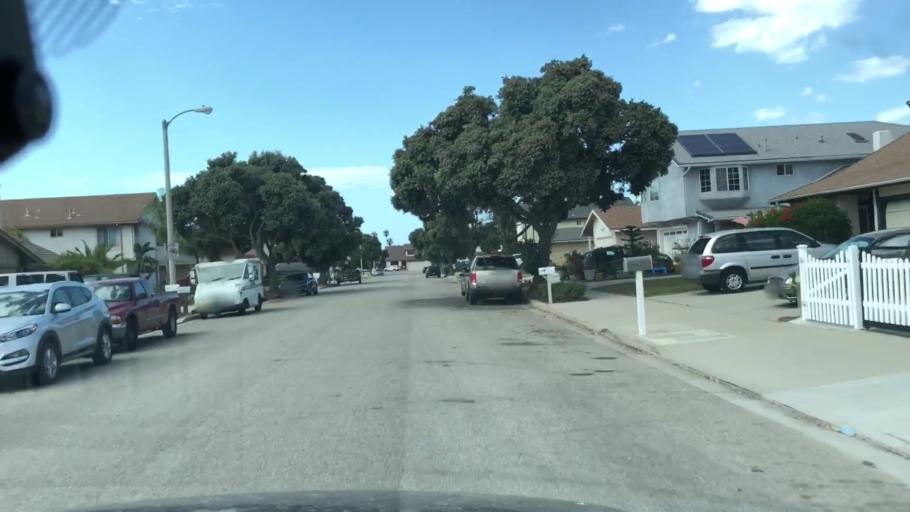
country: US
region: California
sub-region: Ventura County
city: Channel Islands Beach
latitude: 34.1832
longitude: -119.2091
